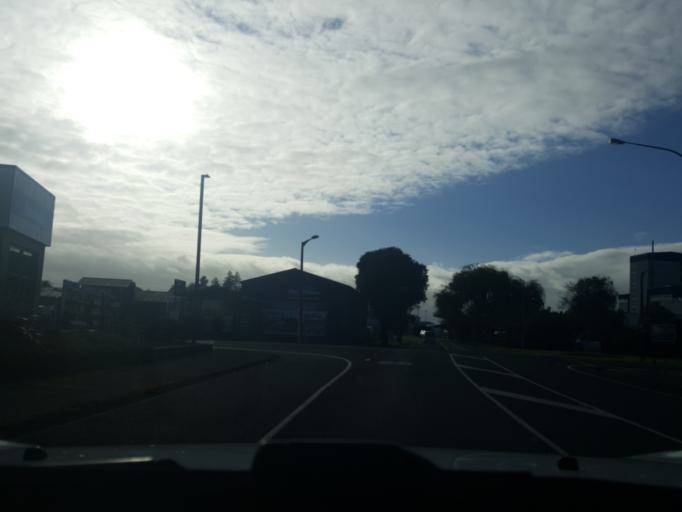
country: NZ
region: Waikato
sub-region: Waipa District
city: Cambridge
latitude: -37.6584
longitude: 175.5310
